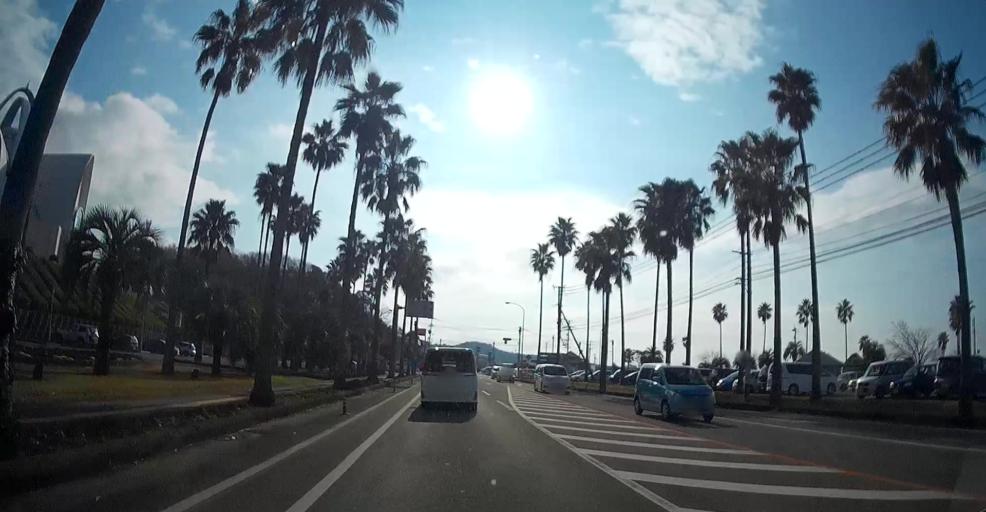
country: JP
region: Kumamoto
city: Yatsushiro
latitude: 32.5767
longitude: 130.4208
